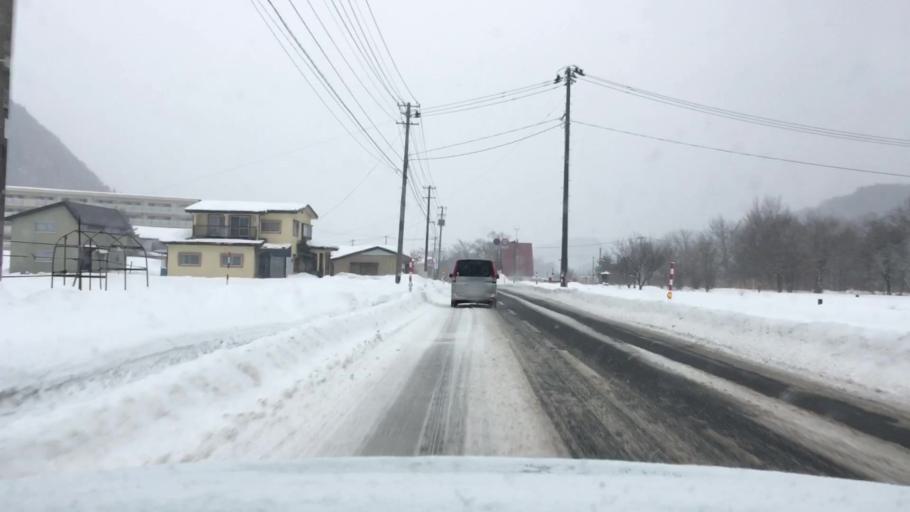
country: JP
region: Akita
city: Hanawa
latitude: 40.0892
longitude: 141.0457
